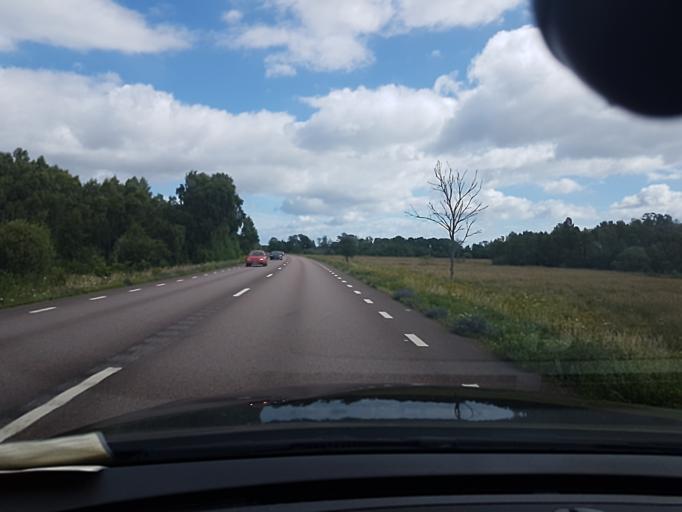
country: SE
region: Kalmar
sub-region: Borgholms Kommun
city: Borgholm
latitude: 57.0749
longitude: 16.9099
